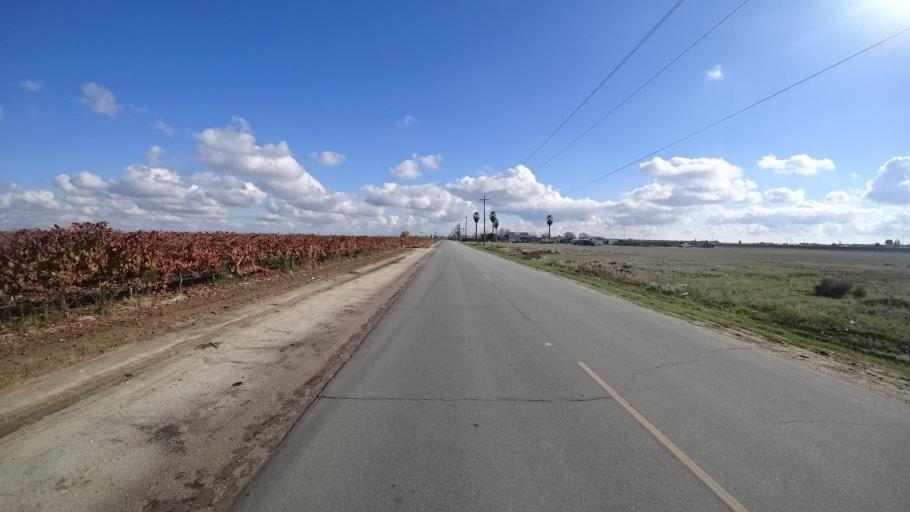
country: US
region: California
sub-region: Kern County
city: McFarland
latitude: 35.6744
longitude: -119.2527
